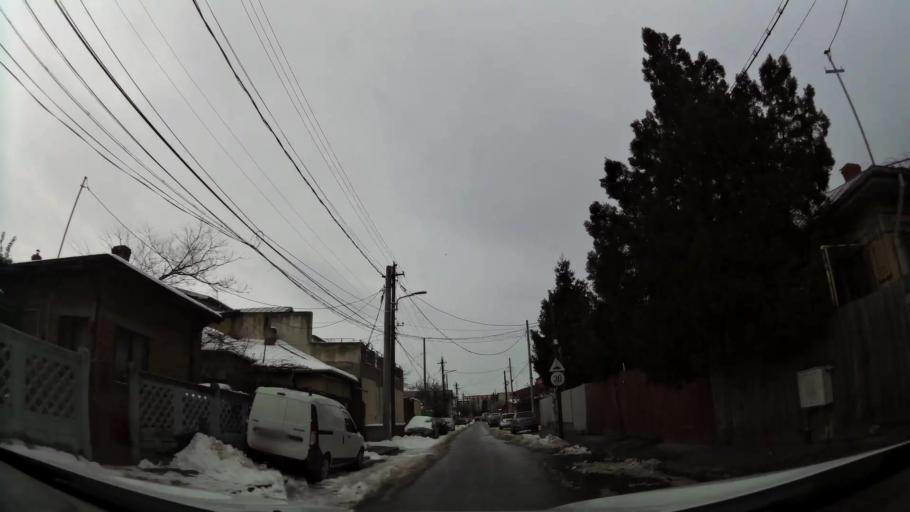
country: RO
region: Bucuresti
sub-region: Municipiul Bucuresti
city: Bucuresti
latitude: 44.4066
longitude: 26.0566
